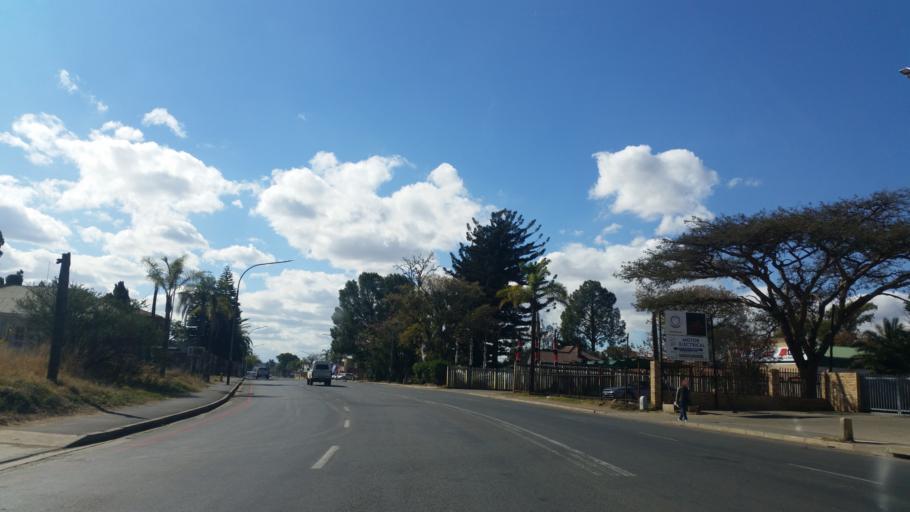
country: ZA
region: KwaZulu-Natal
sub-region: uThukela District Municipality
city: Ladysmith
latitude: -28.5687
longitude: 29.7767
